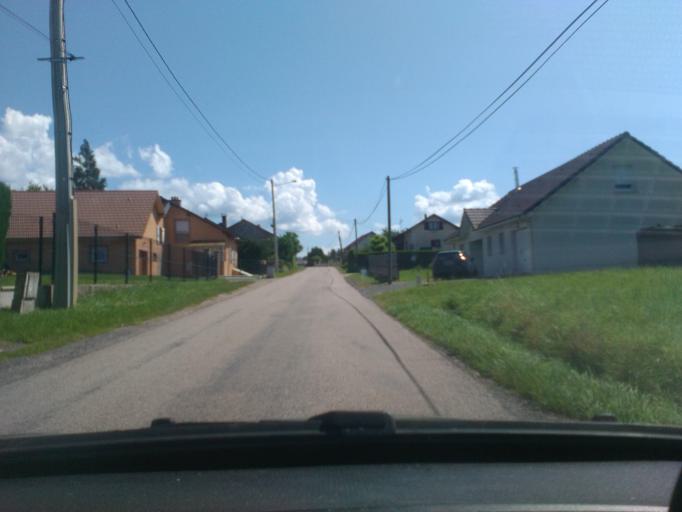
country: FR
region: Lorraine
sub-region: Departement des Vosges
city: Etival-Clairefontaine
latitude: 48.3556
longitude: 6.8647
